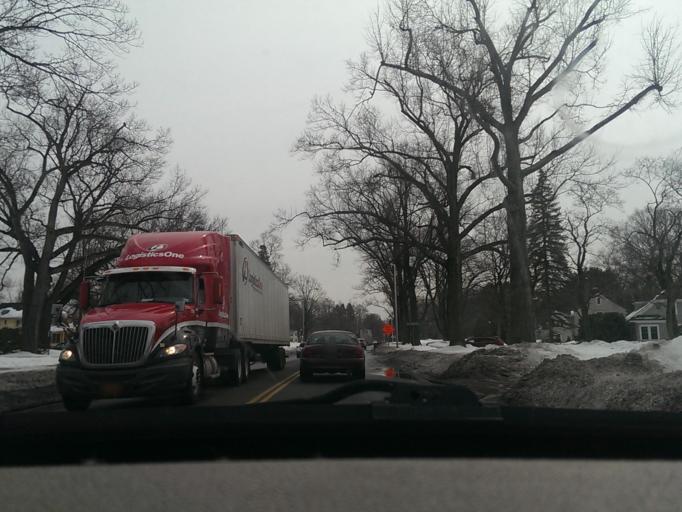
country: US
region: Massachusetts
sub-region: Hampden County
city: Longmeadow
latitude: 42.0672
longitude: -72.5795
